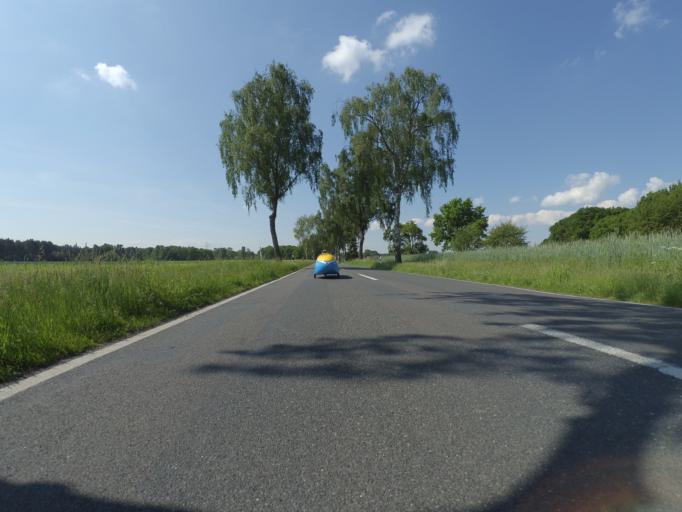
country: DE
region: Lower Saxony
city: Isernhagen Farster Bauerschaft
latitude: 52.5013
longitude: 9.9120
